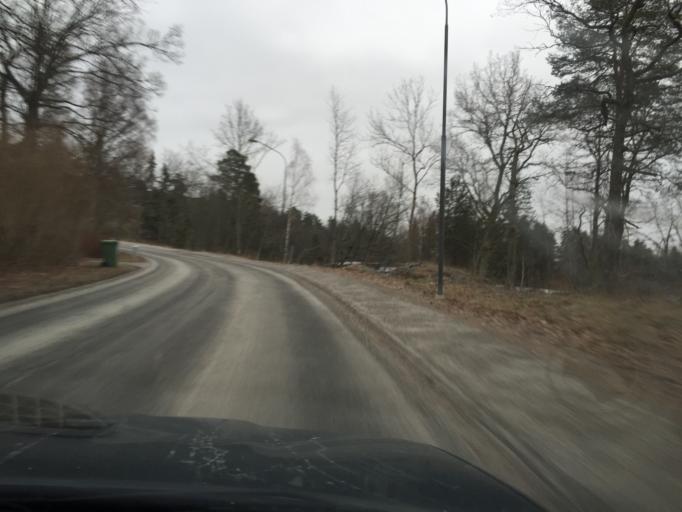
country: SE
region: Stockholm
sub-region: Salems Kommun
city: Ronninge
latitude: 59.1867
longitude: 17.7354
